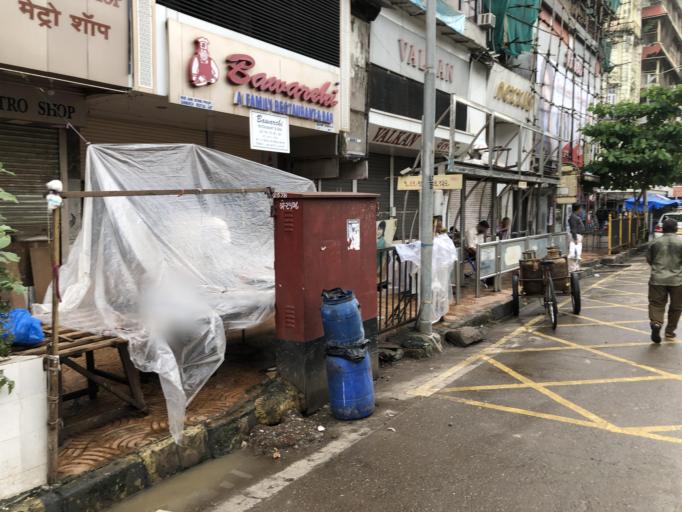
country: IN
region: Maharashtra
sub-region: Raigarh
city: Uran
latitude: 18.9461
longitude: 72.8317
